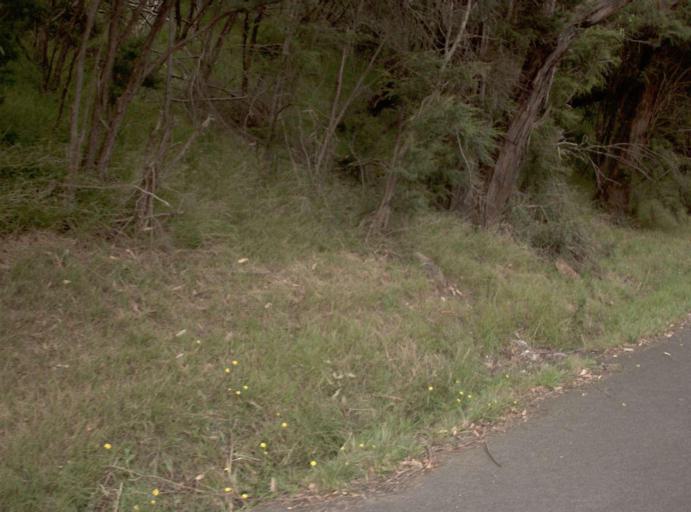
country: AU
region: Victoria
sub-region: Yarra Ranges
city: Badger Creek
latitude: -37.6816
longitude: 145.4872
